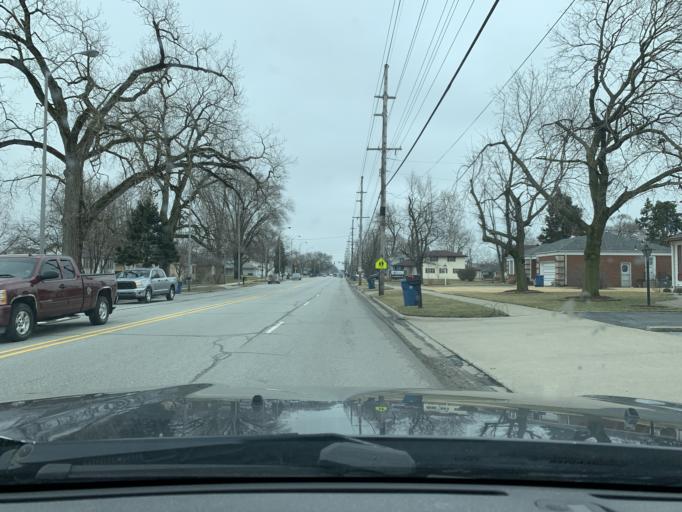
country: US
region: Indiana
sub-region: Lake County
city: Highland
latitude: 41.5446
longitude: -87.4616
